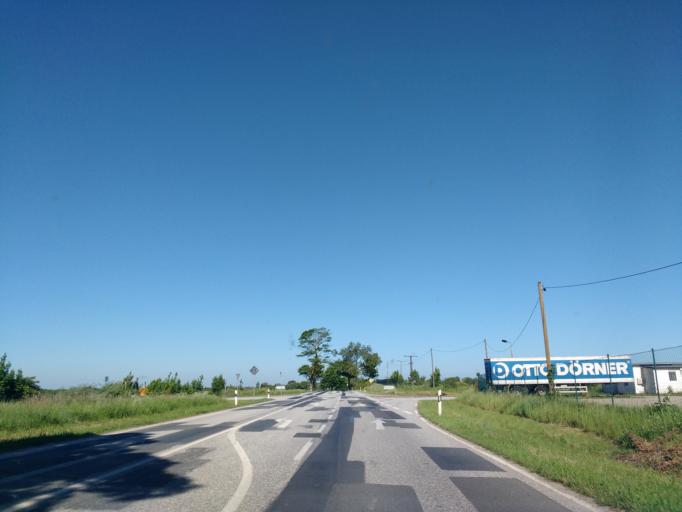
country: DE
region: Mecklenburg-Vorpommern
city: Sellin
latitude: 53.8744
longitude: 11.5872
